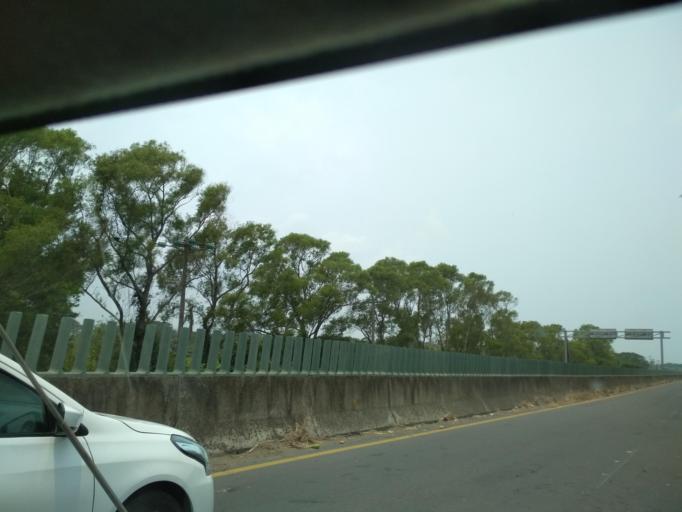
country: MX
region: Veracruz
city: Paso del Toro
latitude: 19.0280
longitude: -96.1413
